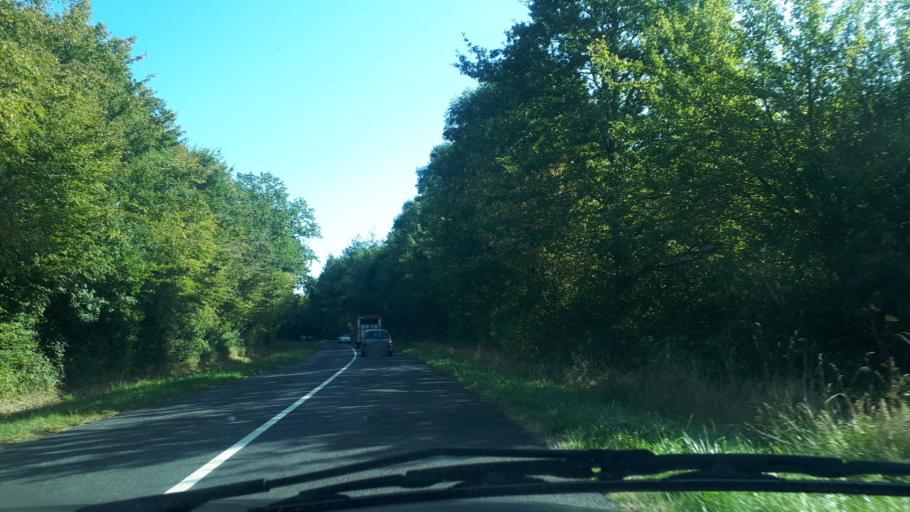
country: FR
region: Centre
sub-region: Departement du Loir-et-Cher
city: Mondoubleau
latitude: 48.0104
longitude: 0.9513
